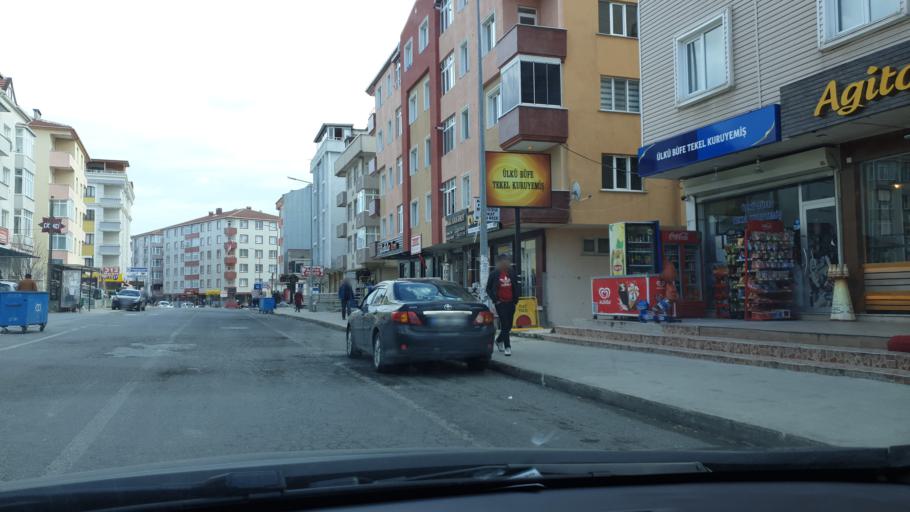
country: TR
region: Tekirdag
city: Cerkezkoey
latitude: 41.2853
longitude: 28.0064
